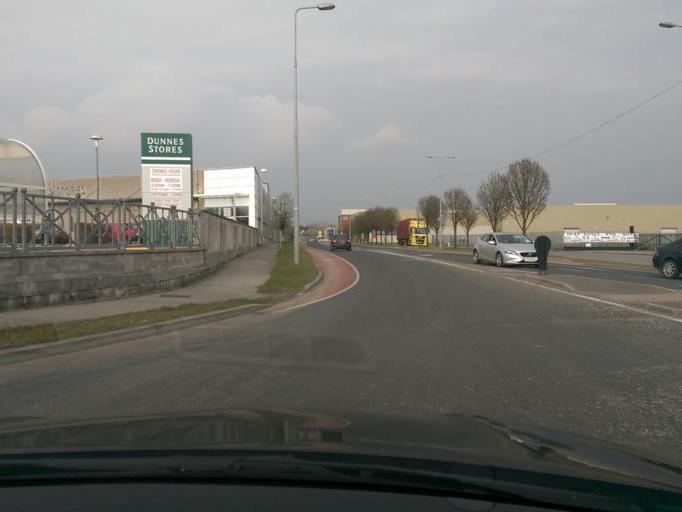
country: IE
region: Connaught
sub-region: Roscommon
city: Roscommon
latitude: 53.6314
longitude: -8.1846
